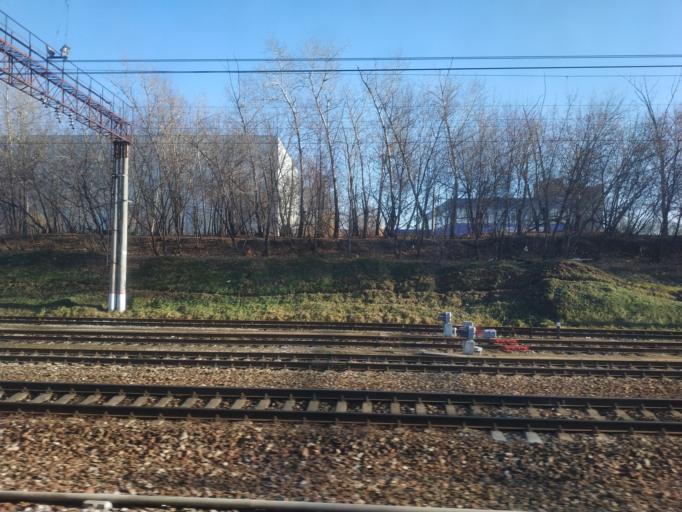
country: RU
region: Moscow
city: Nagornyy
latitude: 55.6508
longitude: 37.6225
